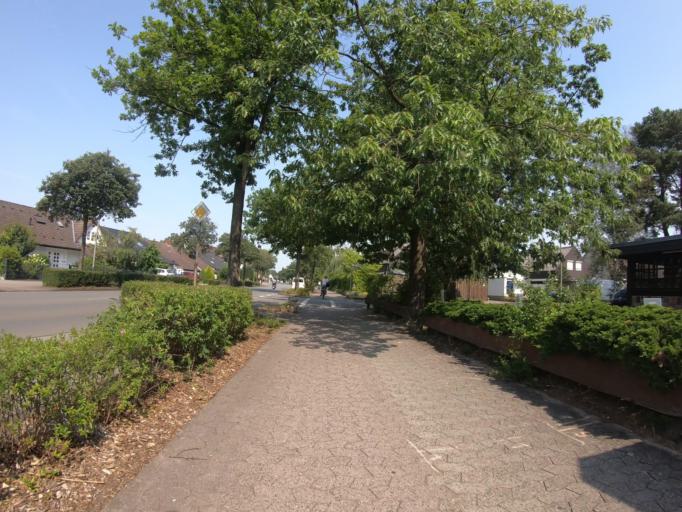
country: DE
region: Lower Saxony
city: Gifhorn
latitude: 52.4738
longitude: 10.5596
